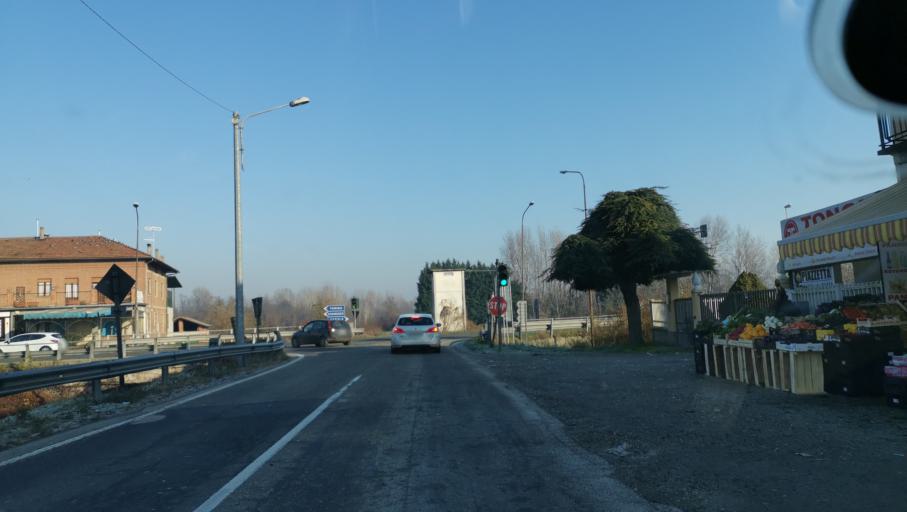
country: IT
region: Piedmont
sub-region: Provincia di Torino
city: San Sebastiano da Po
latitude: 45.1682
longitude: 7.9571
